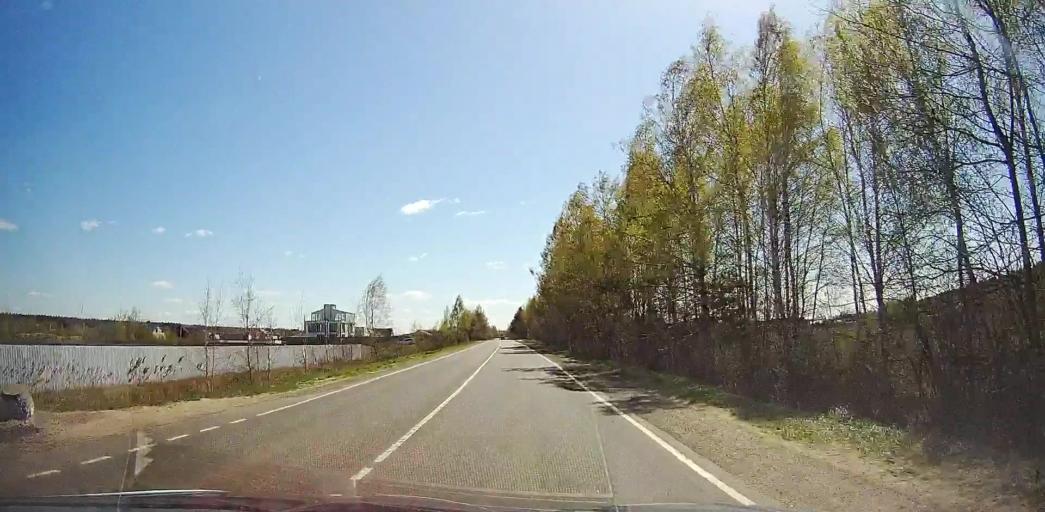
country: RU
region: Moskovskaya
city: Beloozerskiy
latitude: 55.5267
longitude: 38.4315
